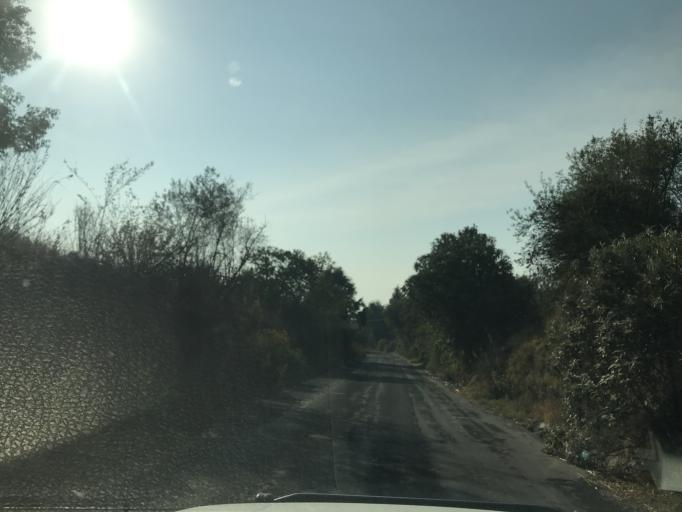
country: MX
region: Puebla
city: San Nicolas de los Ranchos
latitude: 19.0852
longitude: -98.5258
